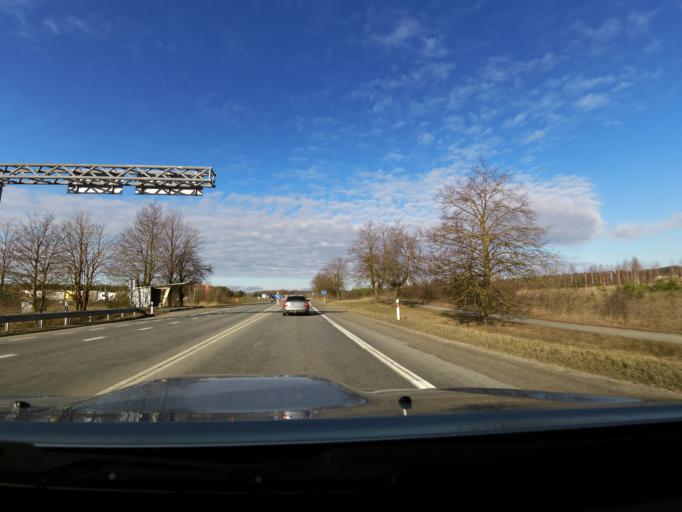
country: LT
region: Panevezys
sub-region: Panevezys City
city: Panevezys
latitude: 55.7343
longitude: 24.2667
